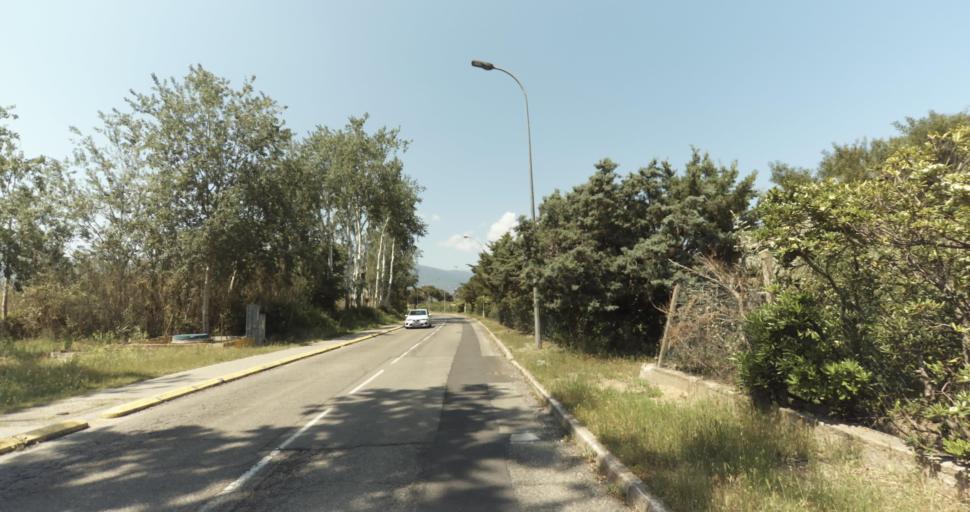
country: FR
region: Corsica
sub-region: Departement de la Haute-Corse
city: Biguglia
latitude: 42.6359
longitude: 9.4617
